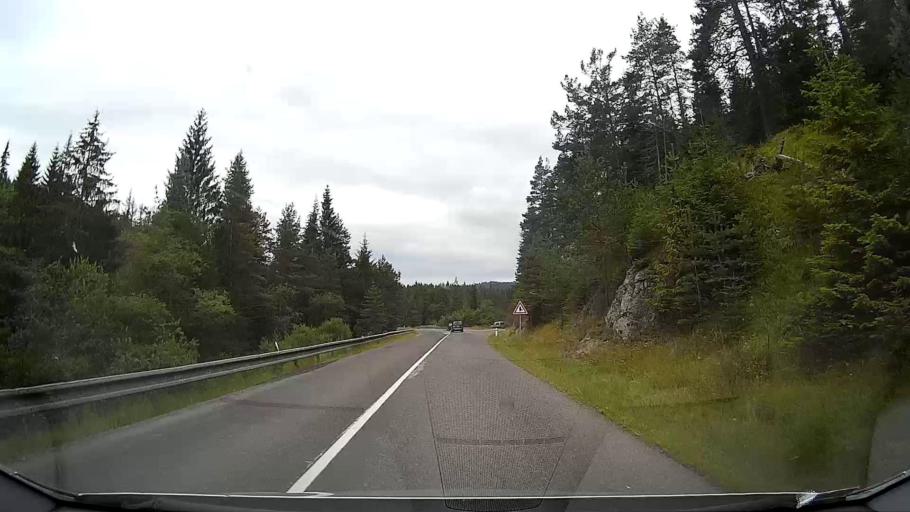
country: SK
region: Kosicky
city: Dobsina
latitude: 48.8807
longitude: 20.2327
